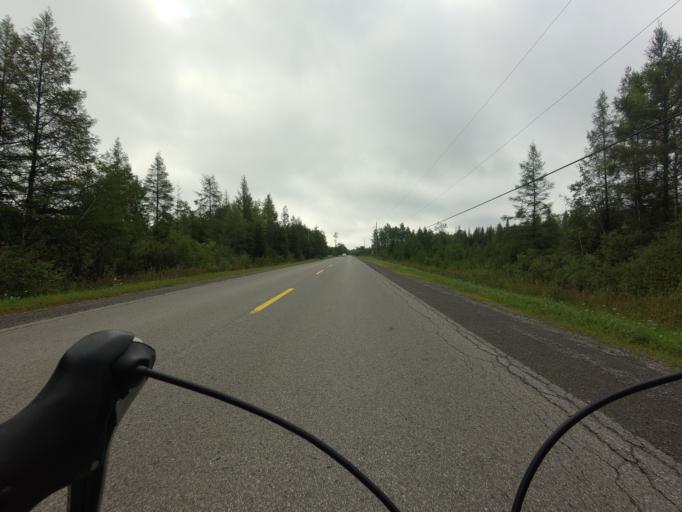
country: CA
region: Ontario
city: Bells Corners
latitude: 45.0735
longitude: -75.7363
